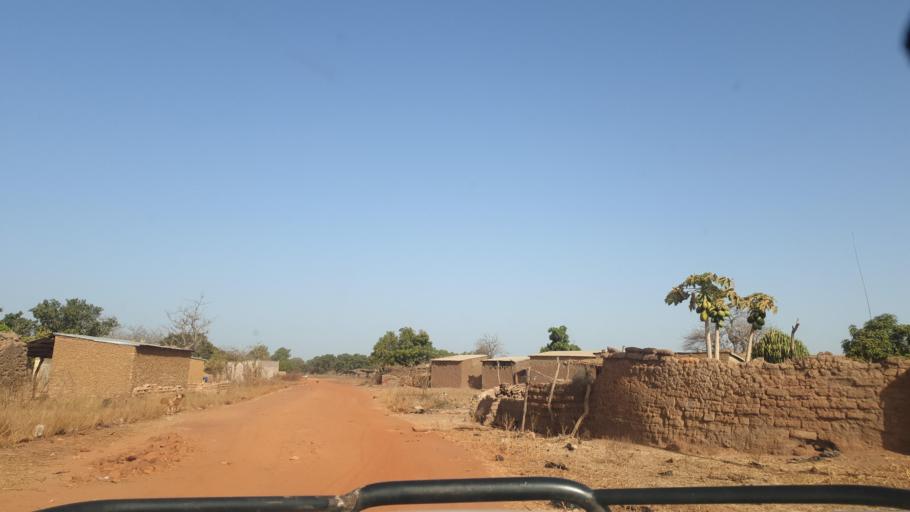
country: ML
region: Sikasso
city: Kolondieba
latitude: 11.7328
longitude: -6.8909
